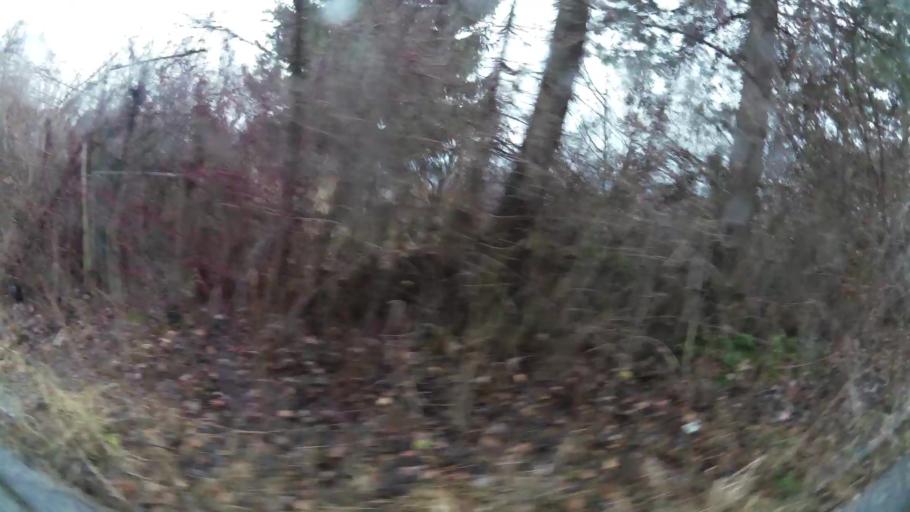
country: BG
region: Sofia-Capital
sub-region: Stolichna Obshtina
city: Sofia
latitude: 42.5988
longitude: 23.3953
